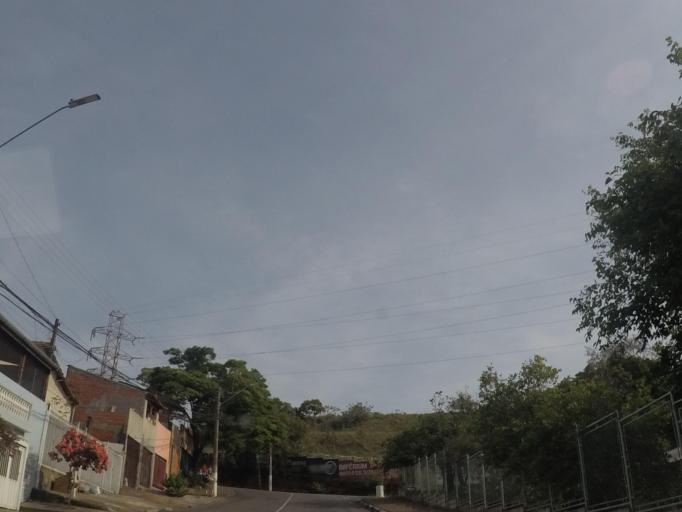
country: BR
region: Sao Paulo
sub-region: Hortolandia
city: Hortolandia
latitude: -22.8636
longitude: -47.1998
